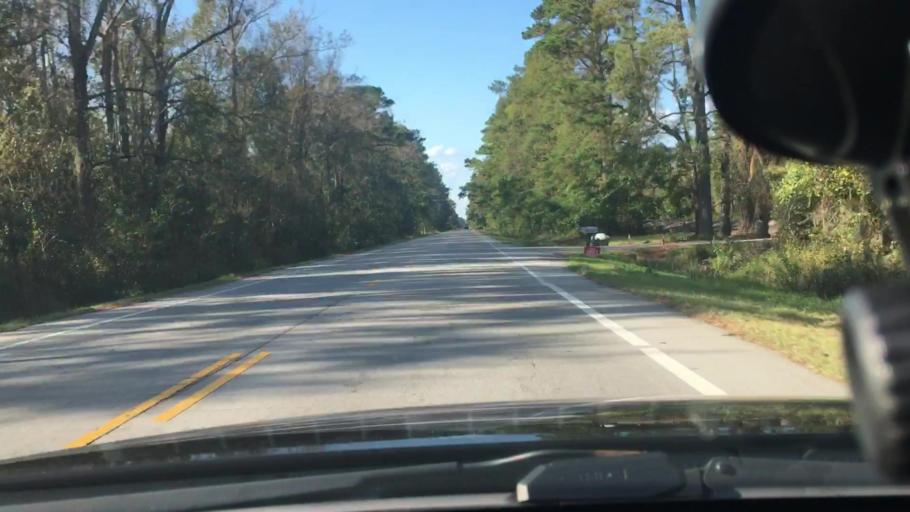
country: US
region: North Carolina
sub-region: Craven County
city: New Bern
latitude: 35.1607
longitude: -77.0384
